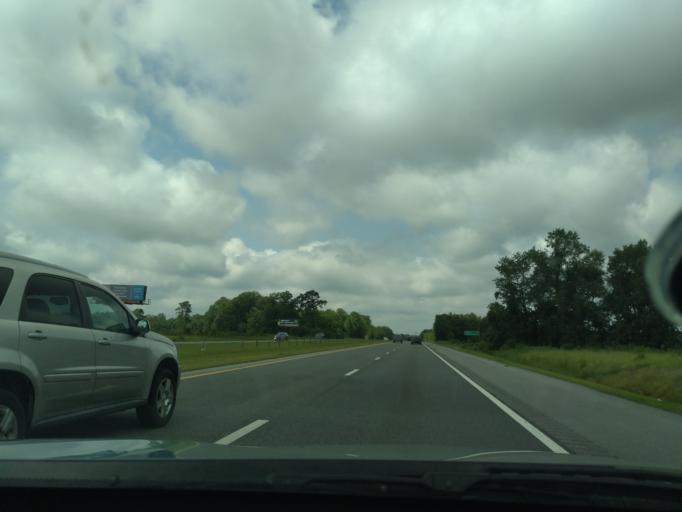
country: US
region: North Carolina
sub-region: Martin County
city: Robersonville
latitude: 35.8337
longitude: -77.2683
